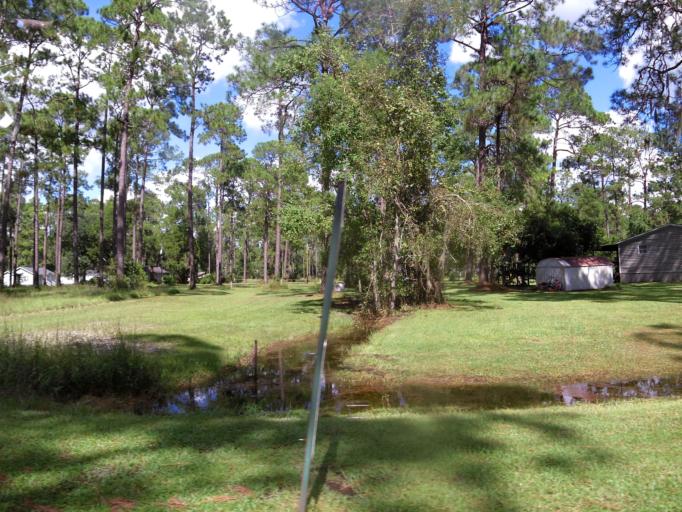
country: US
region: Georgia
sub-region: Clinch County
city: Homerville
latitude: 30.6876
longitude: -82.5637
